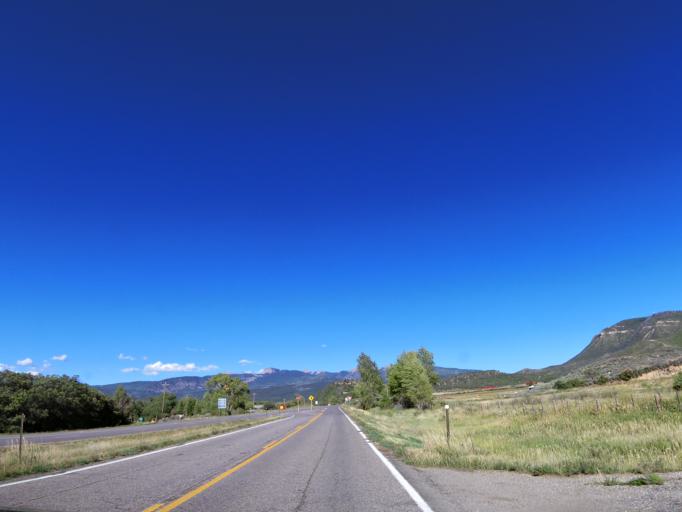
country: US
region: Colorado
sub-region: Montezuma County
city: Mancos
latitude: 37.3477
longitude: -108.2730
